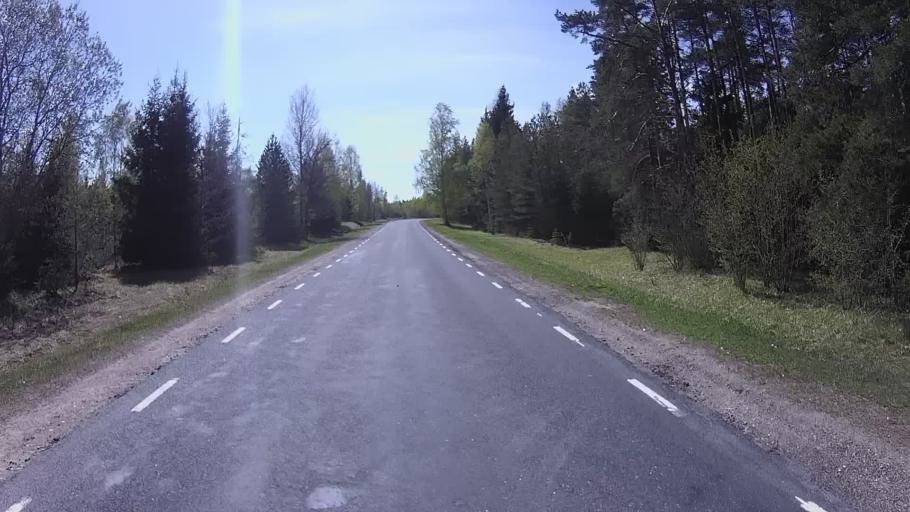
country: EE
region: Laeaene
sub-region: Ridala Parish
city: Uuemoisa
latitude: 59.0384
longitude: 23.8290
